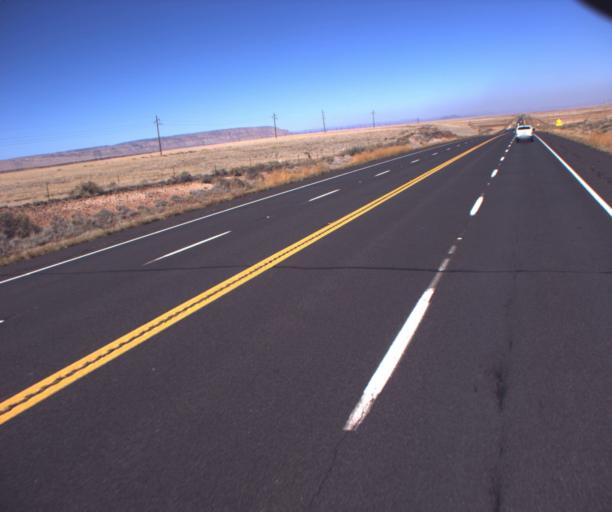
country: US
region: Arizona
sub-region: Coconino County
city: Flagstaff
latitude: 35.6514
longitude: -111.5158
